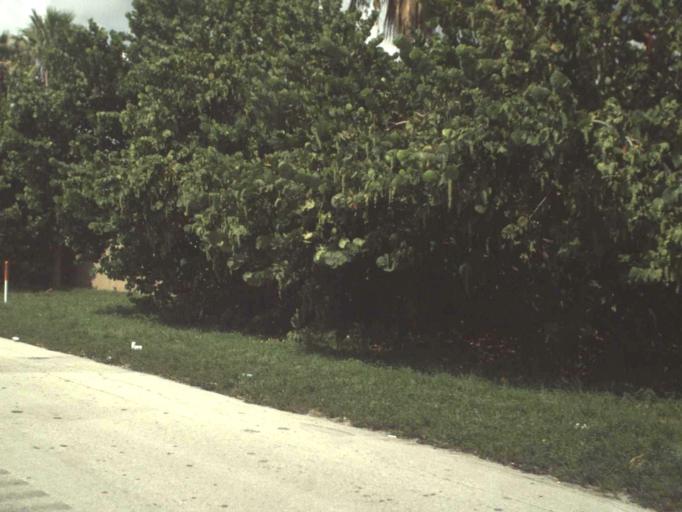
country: US
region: Florida
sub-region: Broward County
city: Tedder
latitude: 26.2958
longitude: -80.1223
